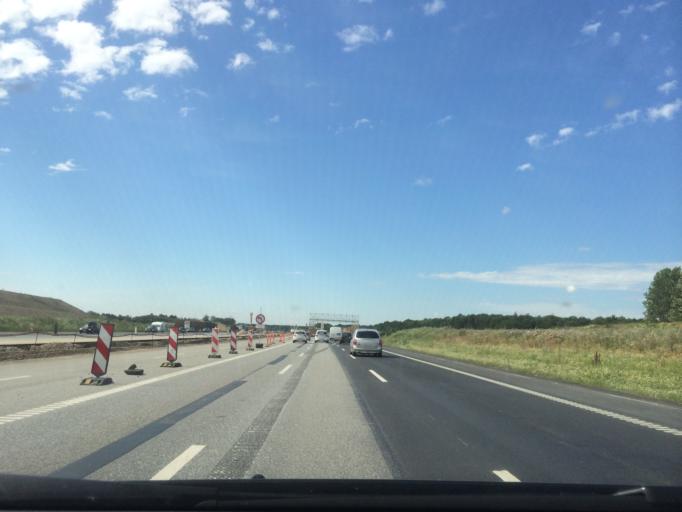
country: DK
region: Zealand
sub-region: Solrod Kommune
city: Solrod Strand
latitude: 55.5655
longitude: 12.2347
